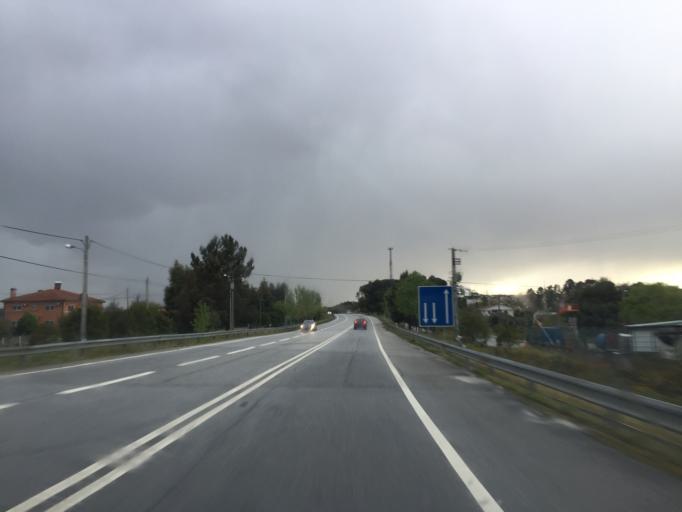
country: PT
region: Viseu
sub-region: Viseu
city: Viseu
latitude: 40.6130
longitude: -7.9579
